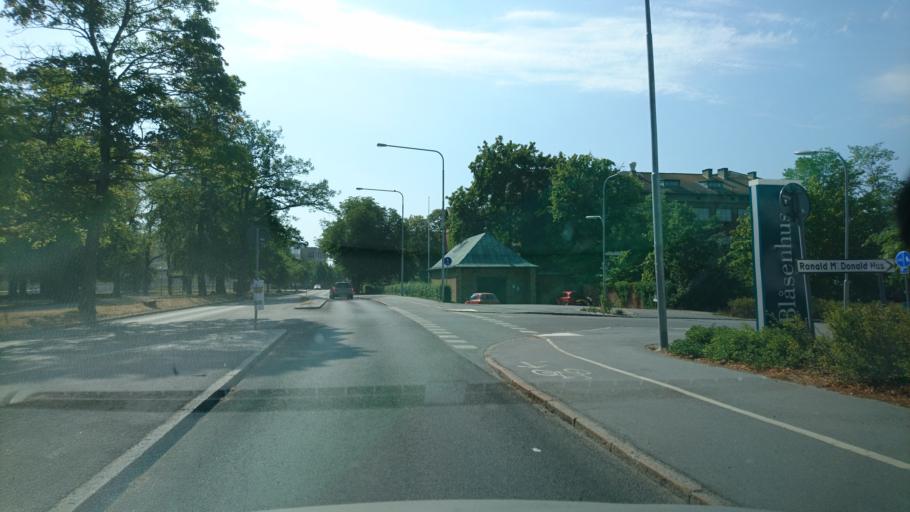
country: SE
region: Uppsala
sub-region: Uppsala Kommun
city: Uppsala
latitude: 59.8504
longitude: 17.6353
